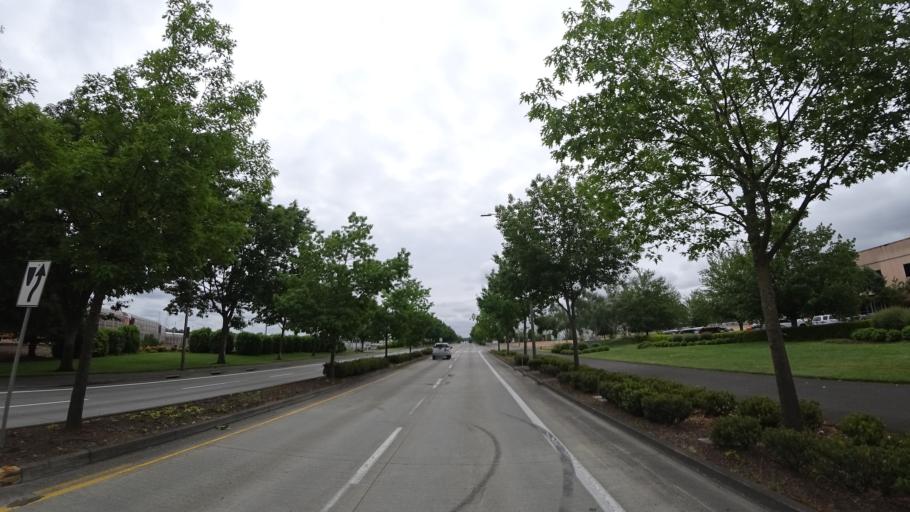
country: US
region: Washington
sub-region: Clark County
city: Lake Shore
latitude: 45.6307
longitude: -122.7461
